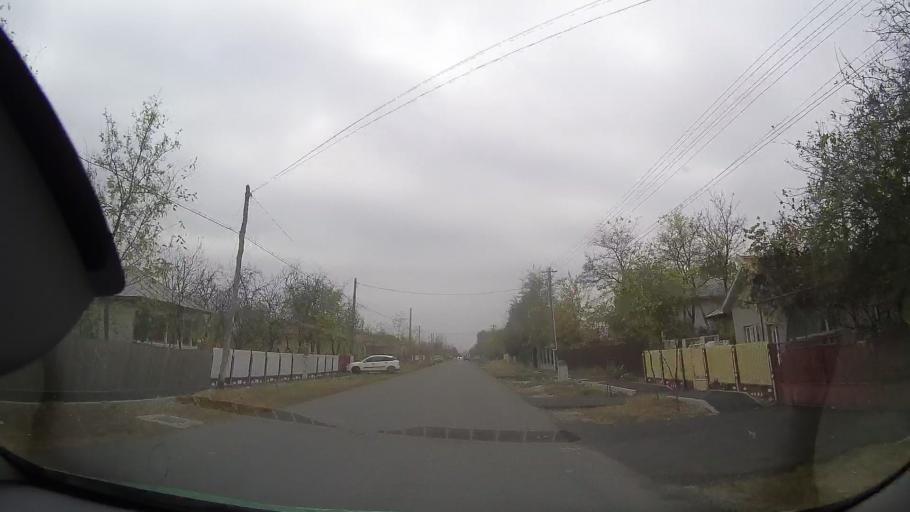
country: RO
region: Buzau
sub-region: Comuna Pogoanele
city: Pogoanele
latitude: 44.9266
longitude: 26.9961
